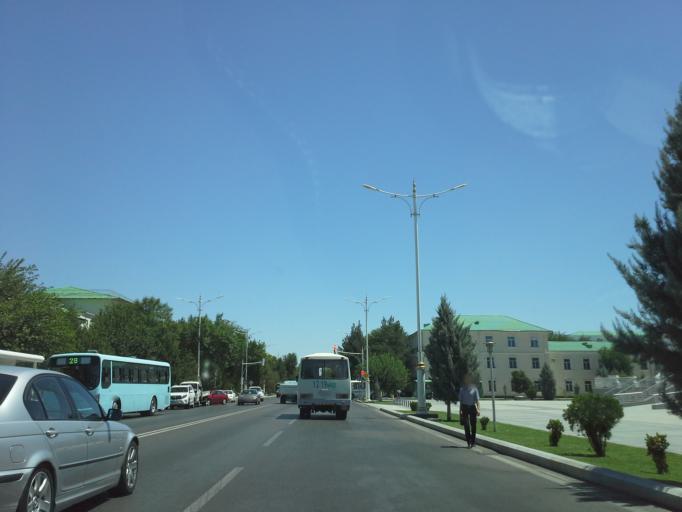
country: TM
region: Ahal
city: Ashgabat
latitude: 37.9501
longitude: 58.3729
